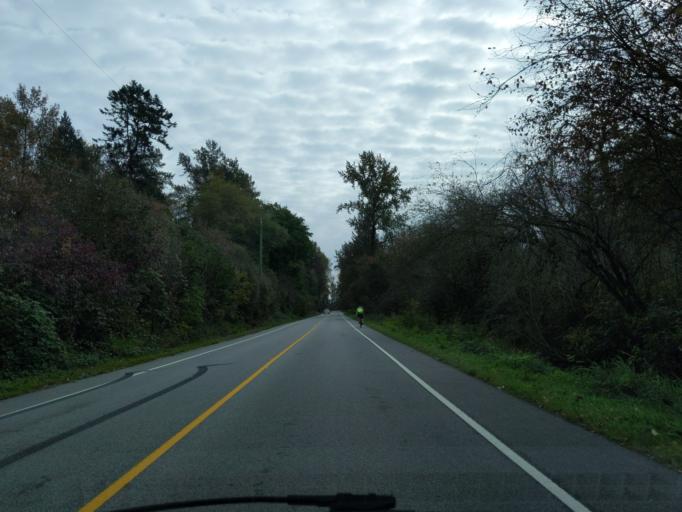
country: CA
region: British Columbia
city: Maple Ridge
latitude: 49.2040
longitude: -122.6003
